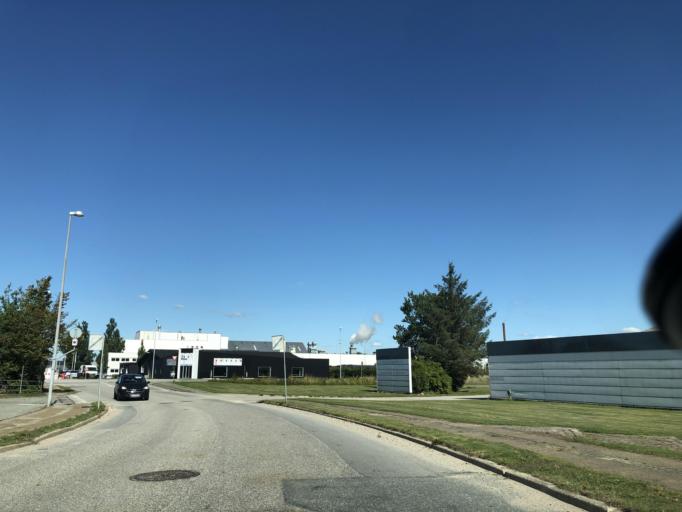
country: DK
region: North Denmark
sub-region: Mariagerfjord Kommune
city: Hobro
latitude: 56.6489
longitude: 9.8024
